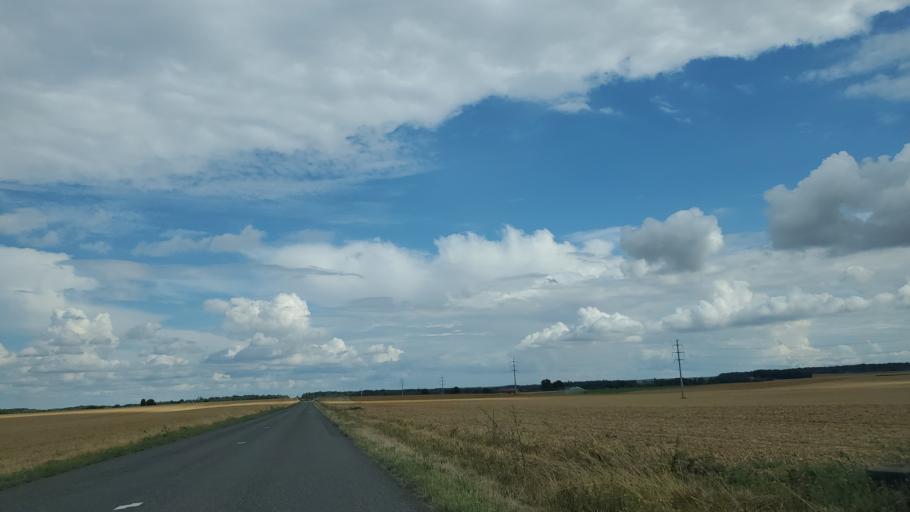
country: FR
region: Ile-de-France
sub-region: Departement de Seine-et-Marne
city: Chailly-en-Brie
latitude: 48.7853
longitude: 3.1431
